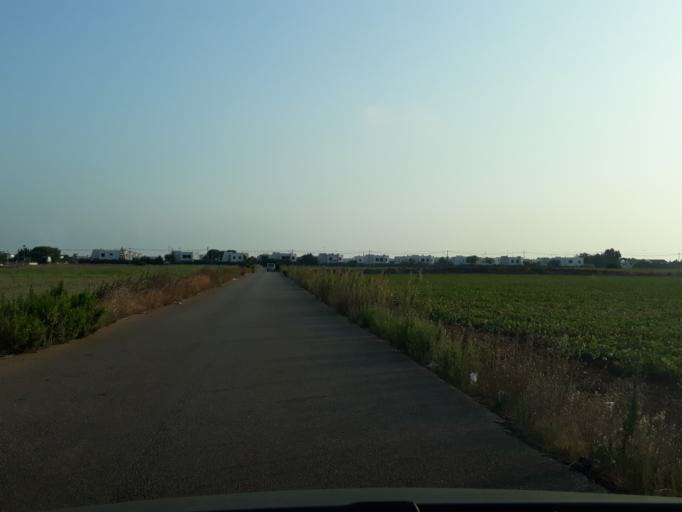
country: IT
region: Apulia
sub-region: Provincia di Brindisi
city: Carovigno
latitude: 40.7489
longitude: 17.7069
